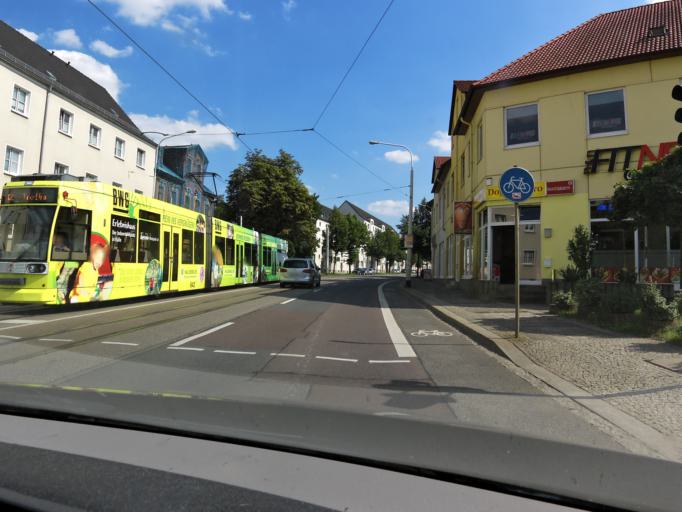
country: DE
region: Saxony-Anhalt
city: Sennewitz
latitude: 51.5127
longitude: 11.9591
